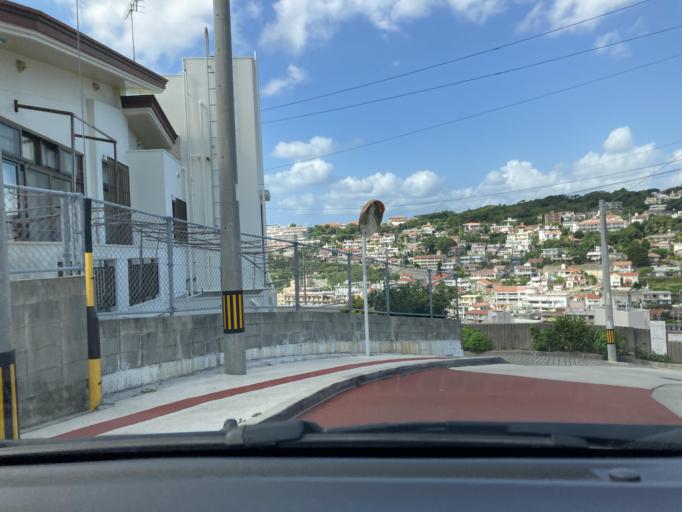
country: JP
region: Okinawa
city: Naha-shi
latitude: 26.2123
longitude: 127.7127
